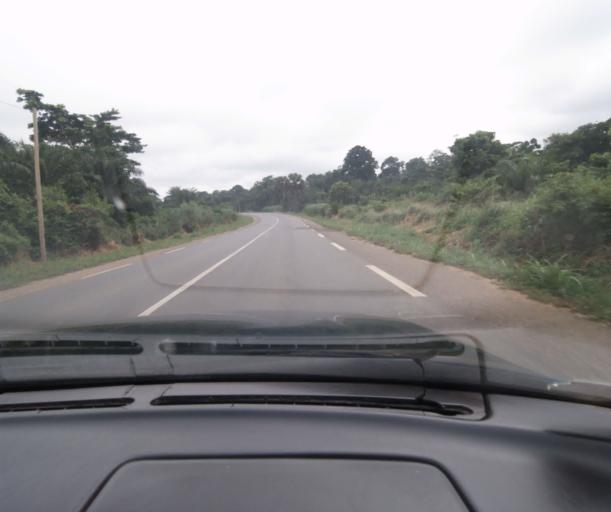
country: CM
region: Centre
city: Saa
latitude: 4.3410
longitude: 11.2837
